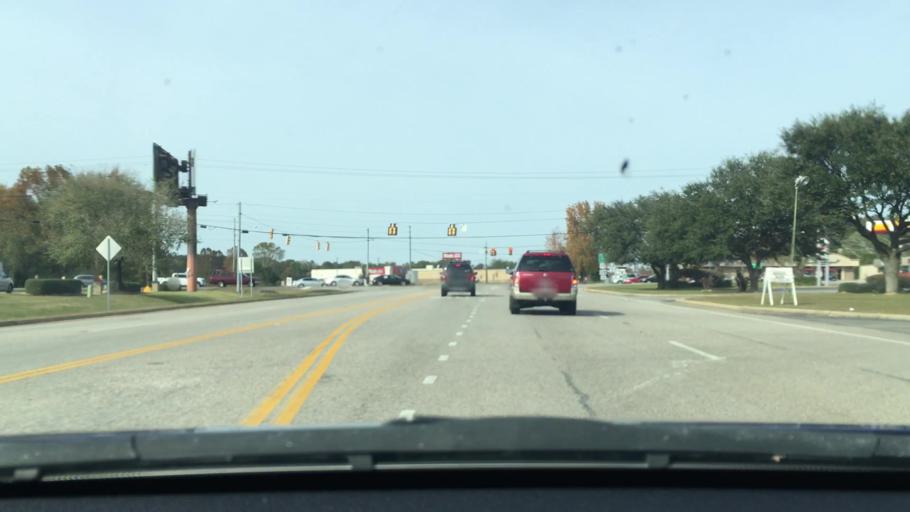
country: US
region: South Carolina
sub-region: Sumter County
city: Oakland
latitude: 33.9505
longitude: -80.4969
